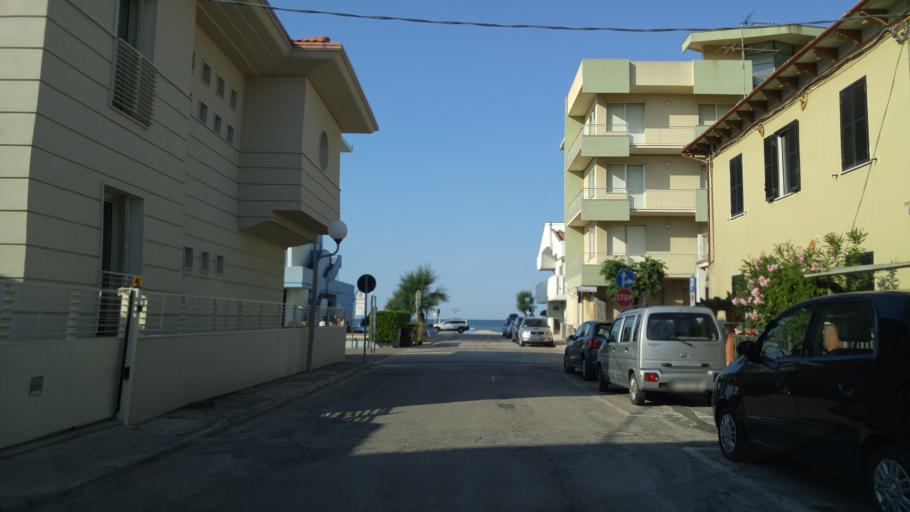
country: IT
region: The Marches
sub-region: Provincia di Pesaro e Urbino
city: Marotta
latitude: 43.7713
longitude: 13.1351
